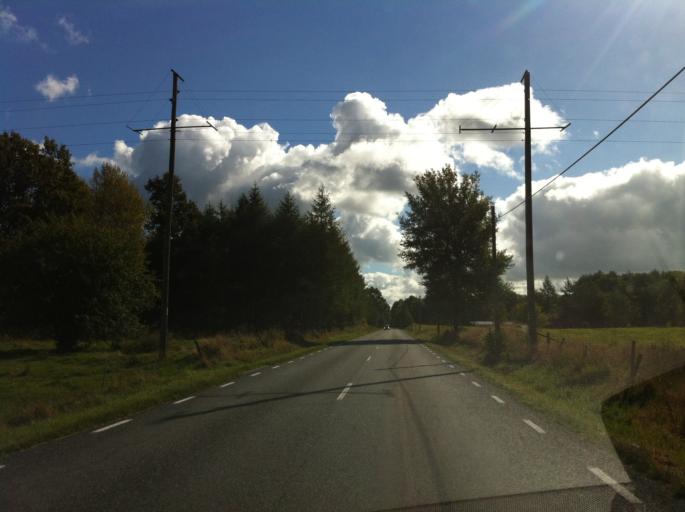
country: SE
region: Skane
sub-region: Kristianstads Kommun
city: Degeberga
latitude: 55.7792
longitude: 13.8866
